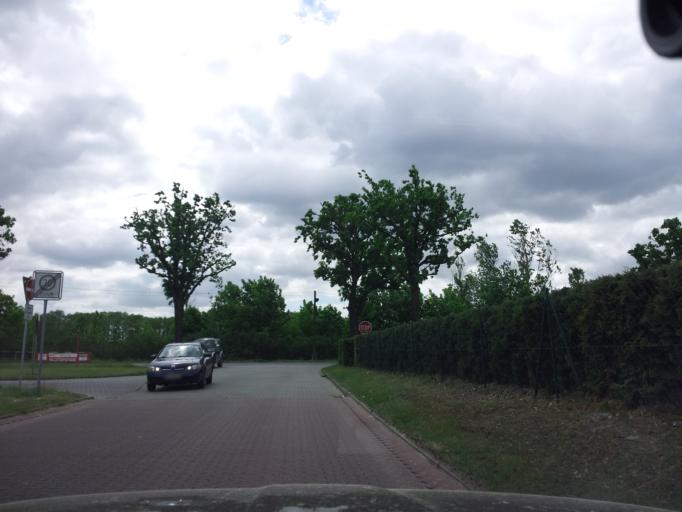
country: DE
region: Brandenburg
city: Treuenbrietzen
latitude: 52.0874
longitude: 12.8489
